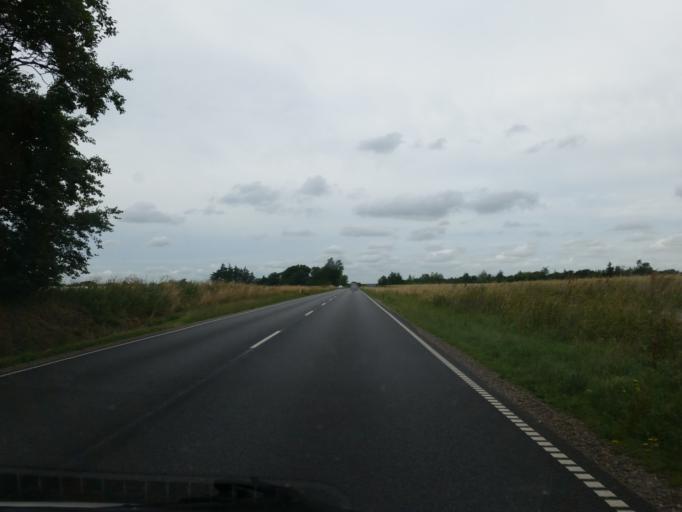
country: DK
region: South Denmark
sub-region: Esbjerg Kommune
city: Ribe
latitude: 55.2569
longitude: 8.7226
